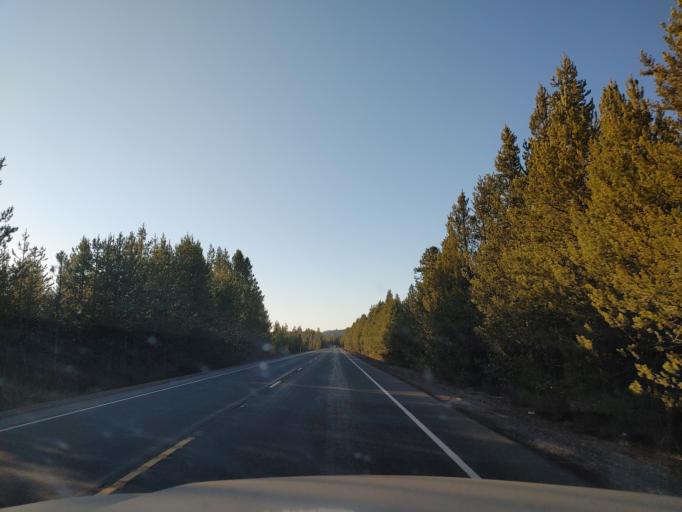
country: US
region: Oregon
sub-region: Deschutes County
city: La Pine
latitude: 43.4149
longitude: -121.8354
